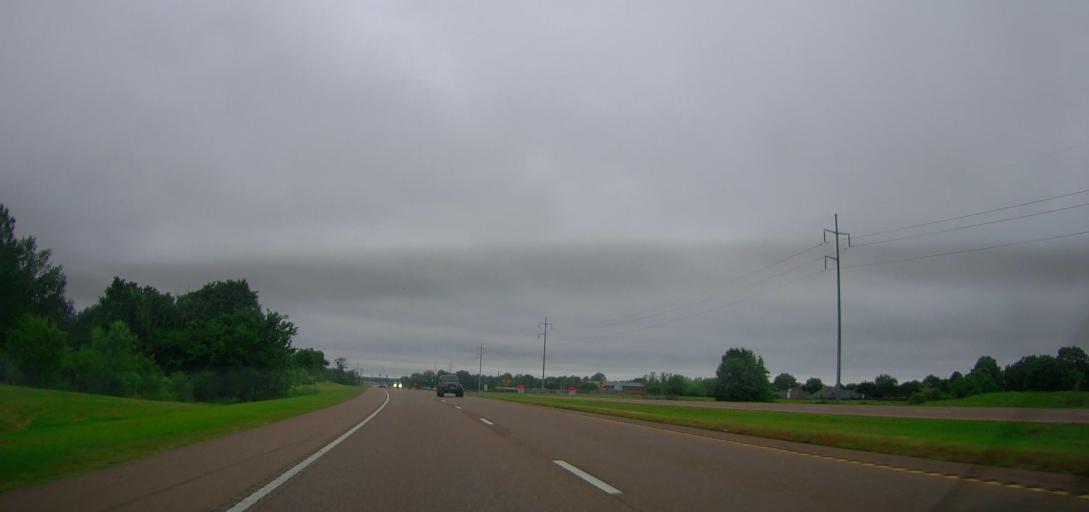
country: US
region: Mississippi
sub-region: De Soto County
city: Olive Branch
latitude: 34.9690
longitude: -89.8089
